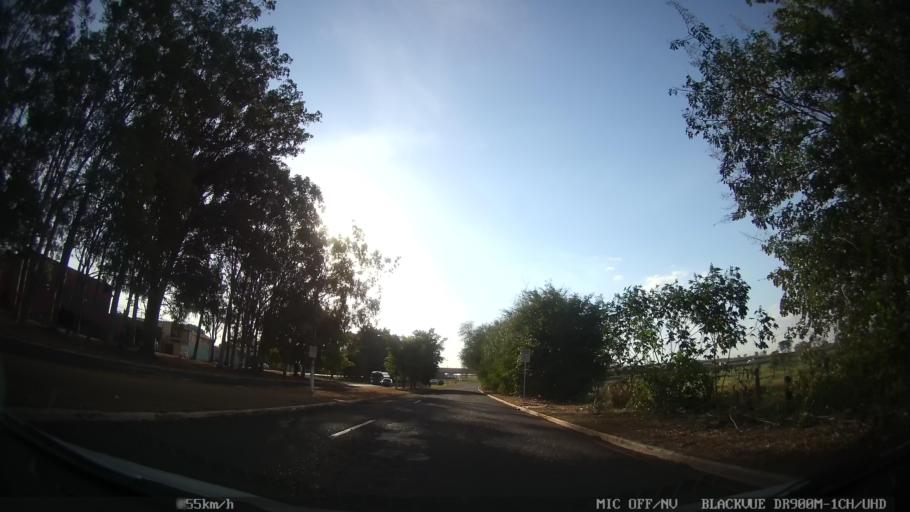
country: BR
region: Sao Paulo
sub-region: Ribeirao Preto
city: Ribeirao Preto
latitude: -21.1295
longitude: -47.8422
